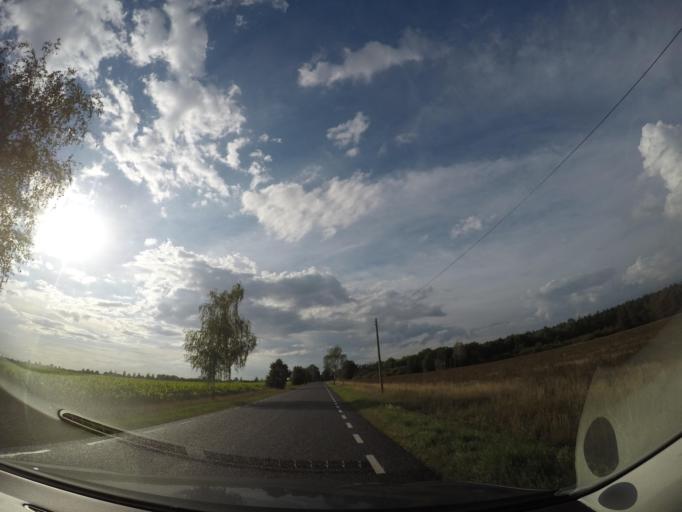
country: DE
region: Saxony-Anhalt
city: Mieste
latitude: 52.5171
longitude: 11.1548
